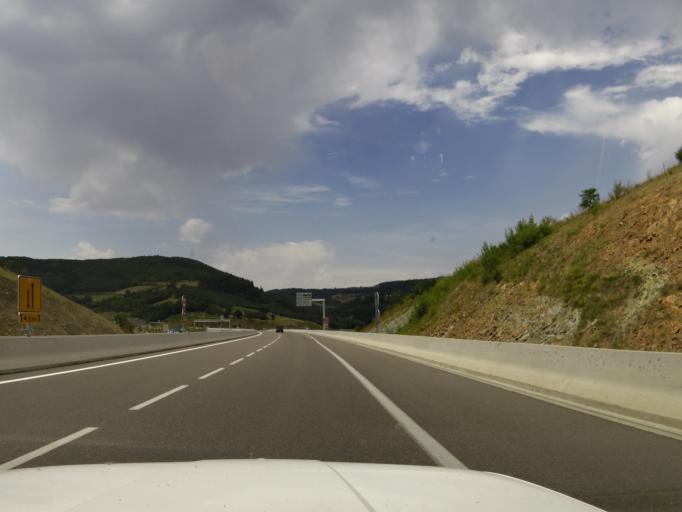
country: FR
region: Rhone-Alpes
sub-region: Departement du Rhone
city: Tarare
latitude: 45.8887
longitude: 4.4148
